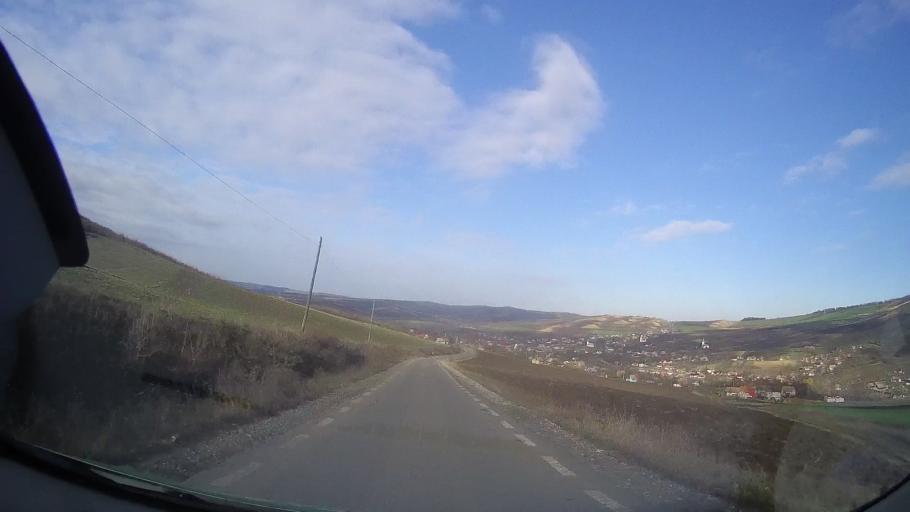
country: RO
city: Barza
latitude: 46.5477
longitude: 24.1468
